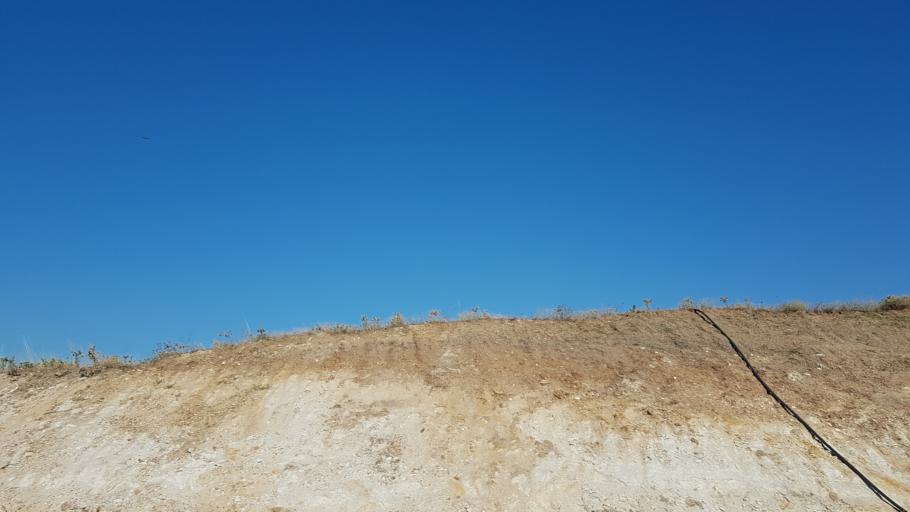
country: TR
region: Balikesir
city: Ertugrul
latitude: 39.6228
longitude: 27.7033
